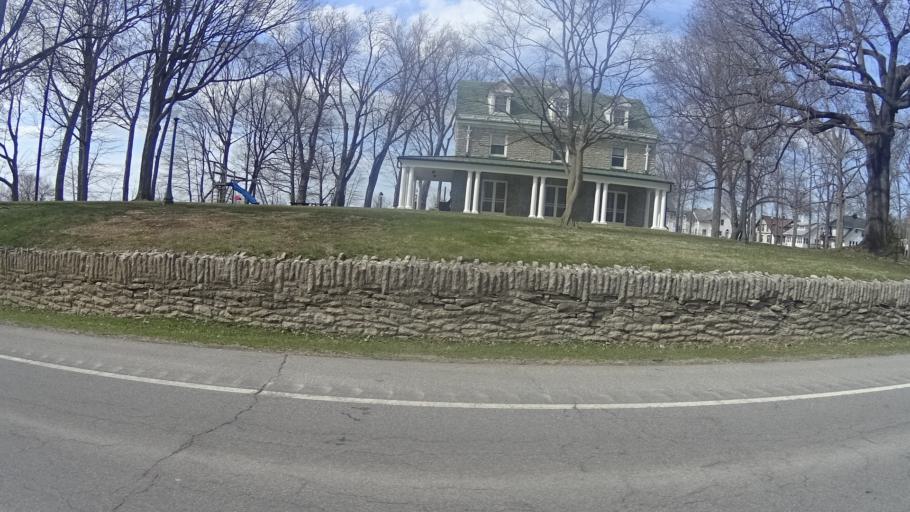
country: US
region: Ohio
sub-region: Erie County
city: Huron
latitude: 41.3820
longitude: -82.4718
